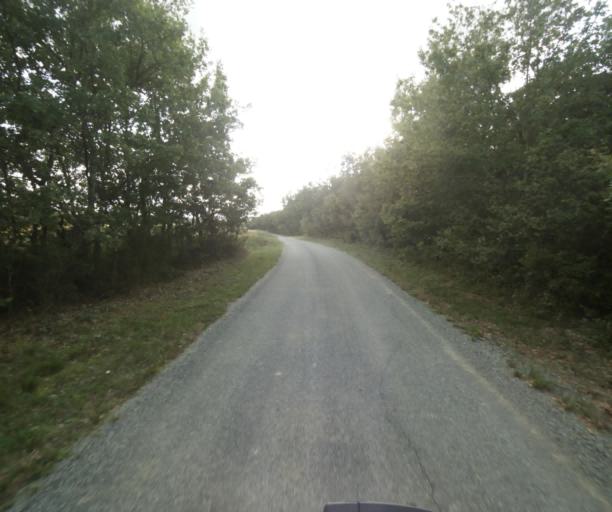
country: FR
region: Midi-Pyrenees
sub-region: Departement de la Haute-Garonne
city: Launac
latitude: 43.8051
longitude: 1.1210
